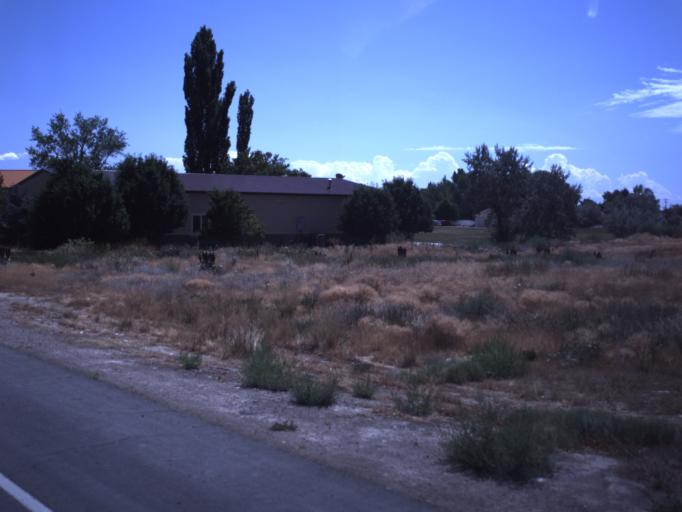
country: US
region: Utah
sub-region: Uintah County
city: Vernal
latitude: 40.4628
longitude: -109.5414
